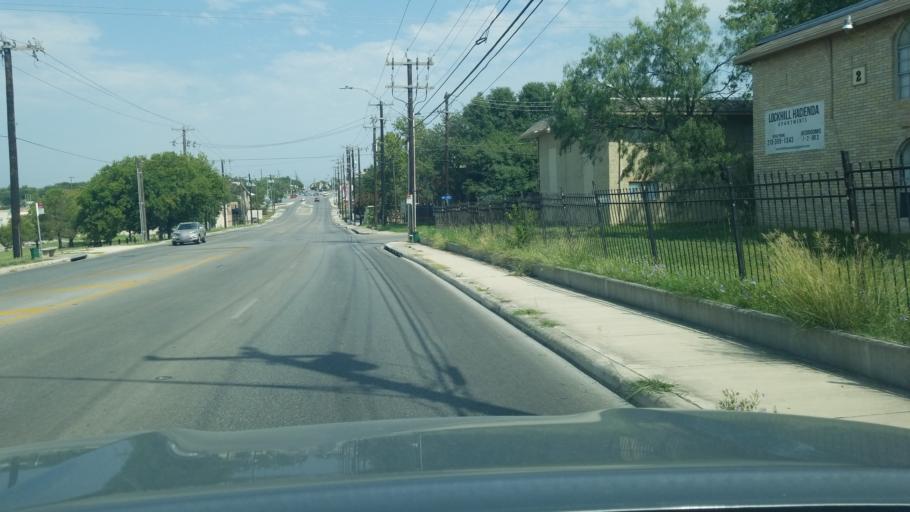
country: US
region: Texas
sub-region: Bexar County
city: Castle Hills
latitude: 29.5383
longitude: -98.5246
